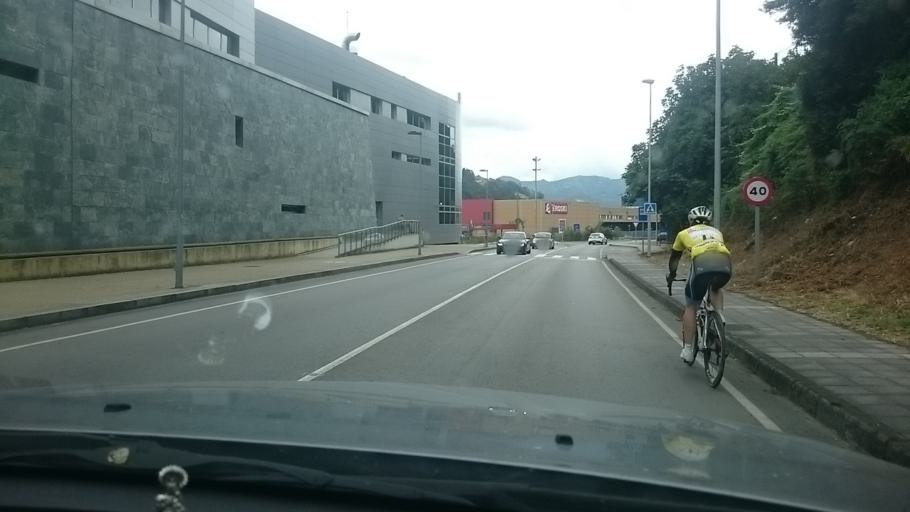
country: ES
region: Asturias
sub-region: Province of Asturias
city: Mieres
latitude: 43.2264
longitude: -5.7809
